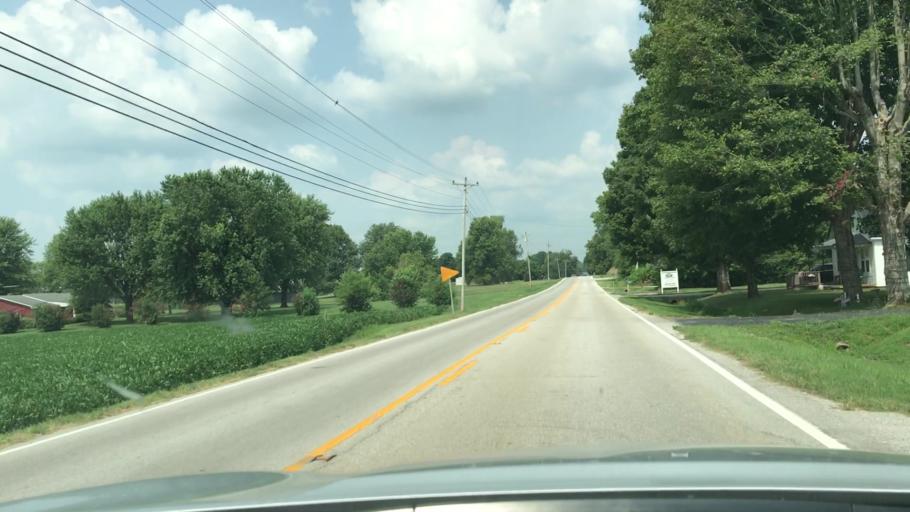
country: US
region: Kentucky
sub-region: Todd County
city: Elkton
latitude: 36.8055
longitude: -87.1286
